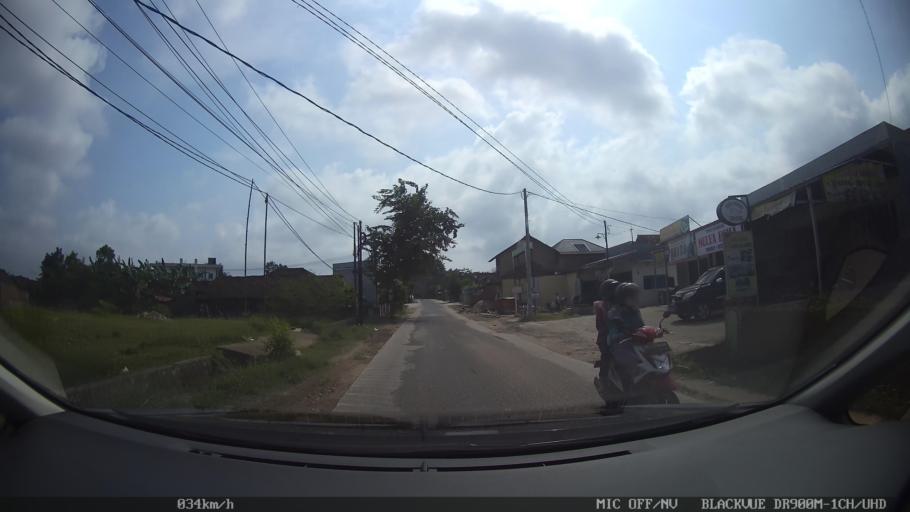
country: ID
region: Lampung
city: Kedaton
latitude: -5.3427
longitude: 105.2705
